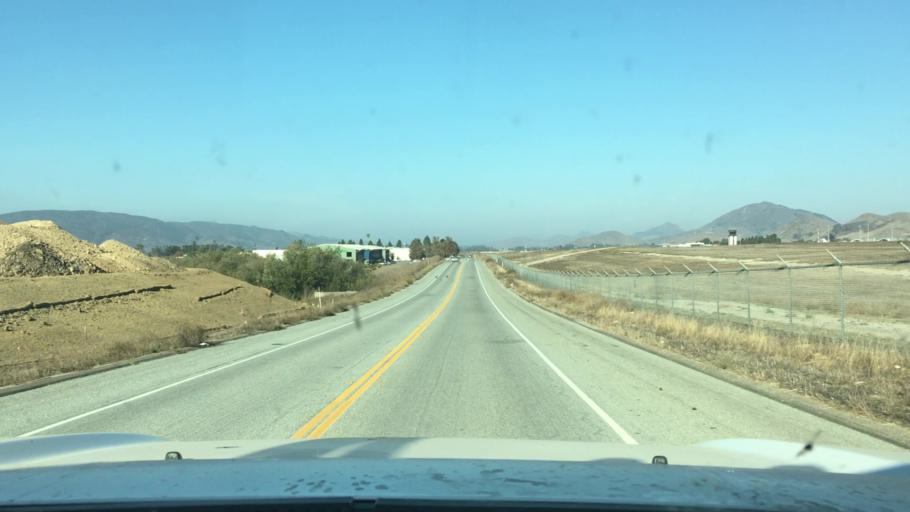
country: US
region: California
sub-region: San Luis Obispo County
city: San Luis Obispo
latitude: 35.2314
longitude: -120.6327
